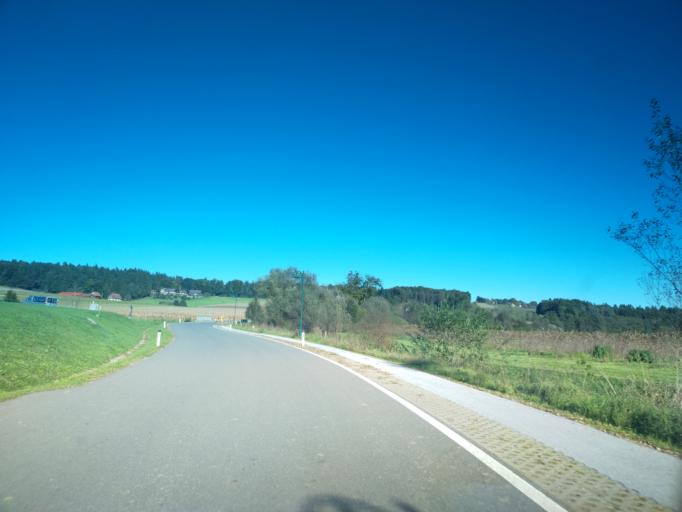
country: AT
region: Styria
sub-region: Politischer Bezirk Deutschlandsberg
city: Rassach
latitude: 46.8562
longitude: 15.2986
